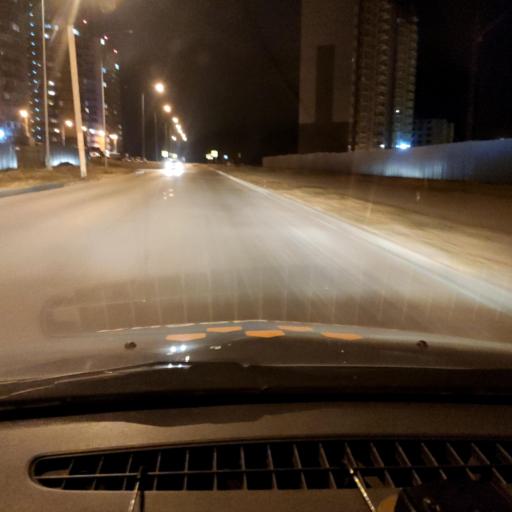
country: RU
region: Voronezj
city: Shilovo
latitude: 51.5686
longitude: 39.1221
